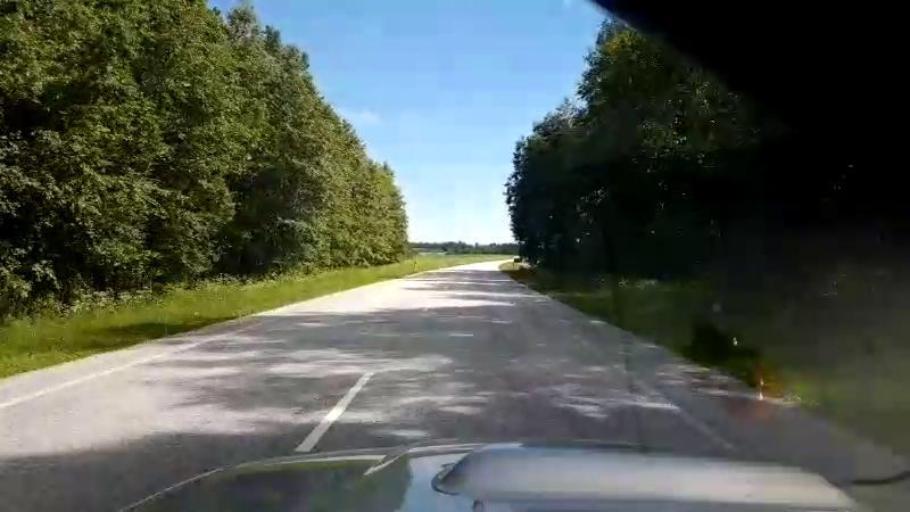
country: EE
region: Laeaene-Virumaa
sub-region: Rakke vald
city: Rakke
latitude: 58.9594
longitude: 26.1650
